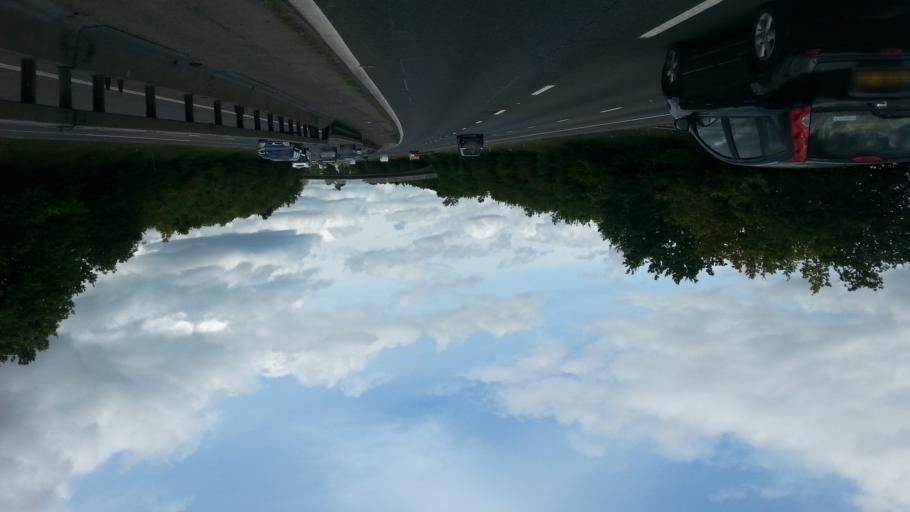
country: GB
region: England
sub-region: Essex
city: Little Hallingbury
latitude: 51.8079
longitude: 0.1770
